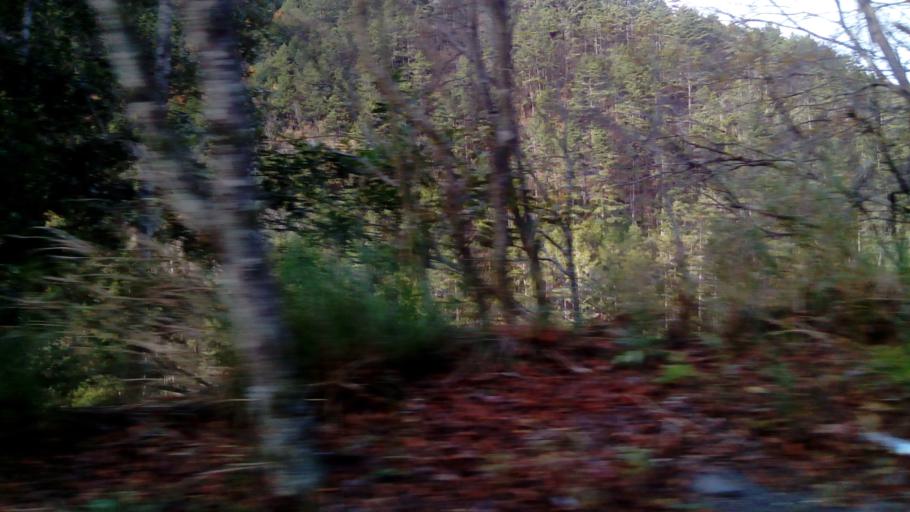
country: TW
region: Taiwan
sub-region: Hualien
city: Hualian
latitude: 24.3488
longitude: 121.3182
